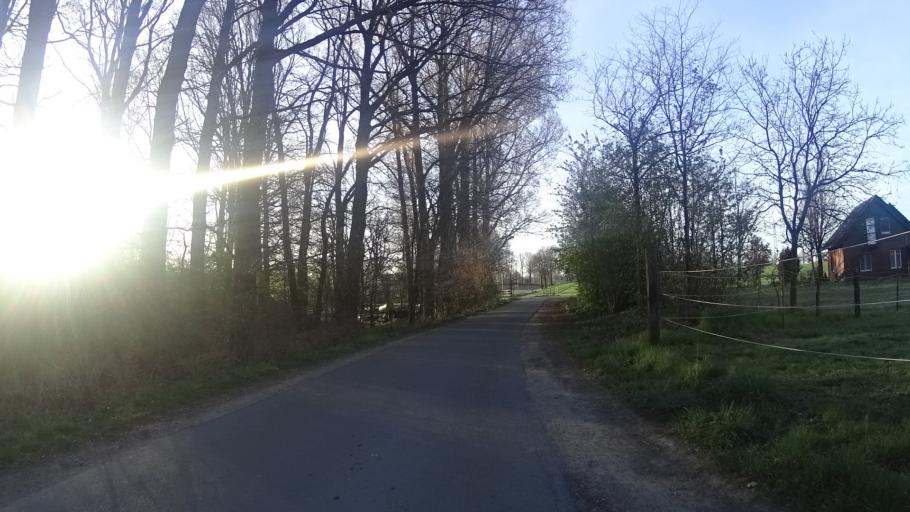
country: DE
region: North Rhine-Westphalia
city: Emsdetten
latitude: 52.2058
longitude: 7.5222
